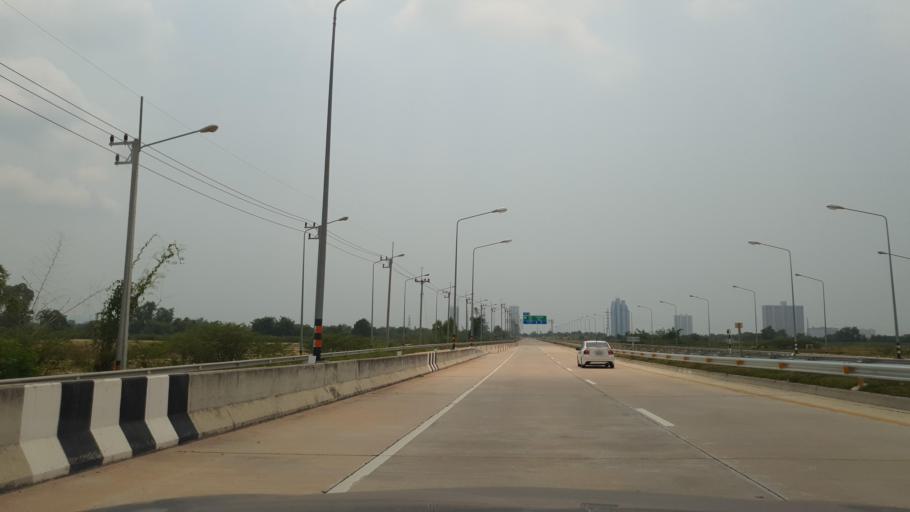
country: TH
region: Chon Buri
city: Phatthaya
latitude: 12.8361
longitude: 100.9334
